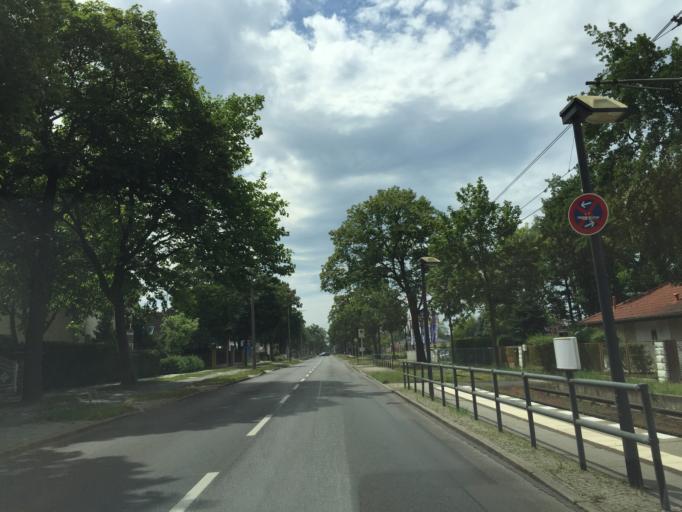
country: DE
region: Berlin
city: Mahlsdorf
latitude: 52.4910
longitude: 13.6077
